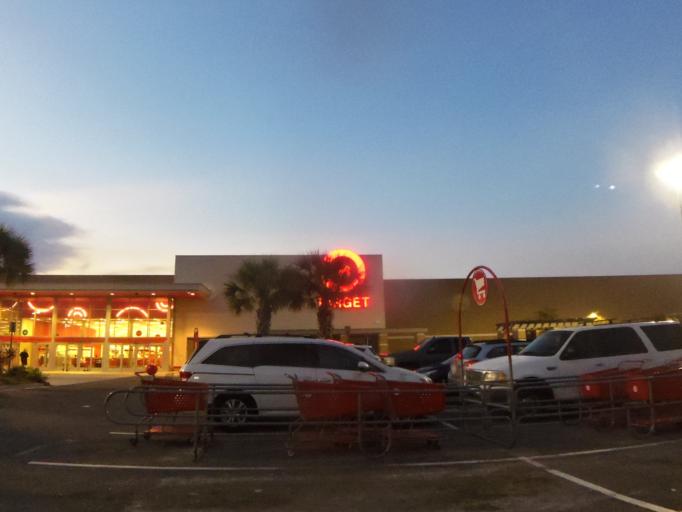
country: US
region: Florida
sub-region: Nassau County
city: Yulee
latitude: 30.6297
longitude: -81.5539
